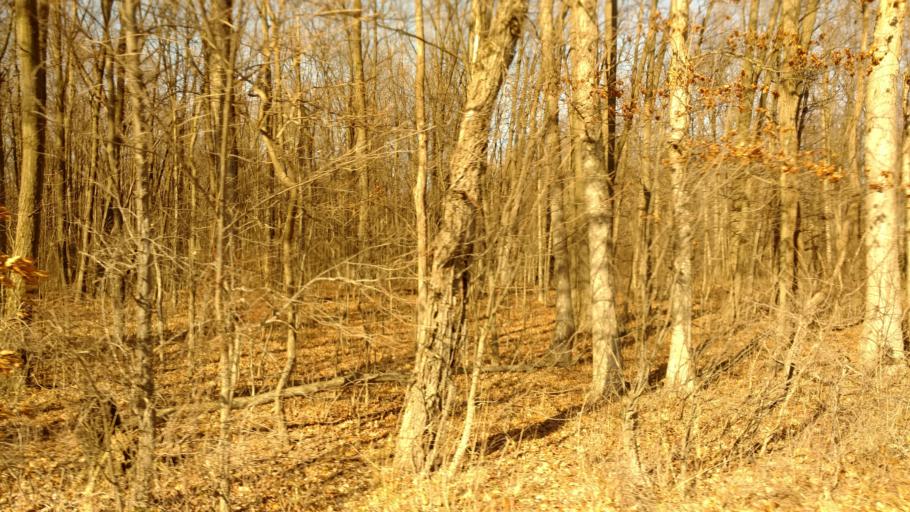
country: US
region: Ohio
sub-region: Wyandot County
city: Upper Sandusky
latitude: 40.7023
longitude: -83.2288
